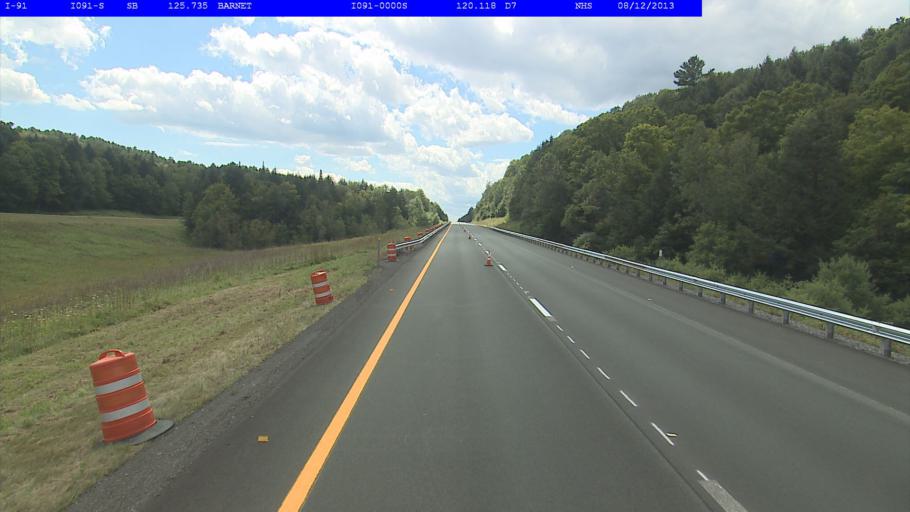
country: US
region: Vermont
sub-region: Caledonia County
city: Saint Johnsbury
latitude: 44.3626
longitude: -72.0321
